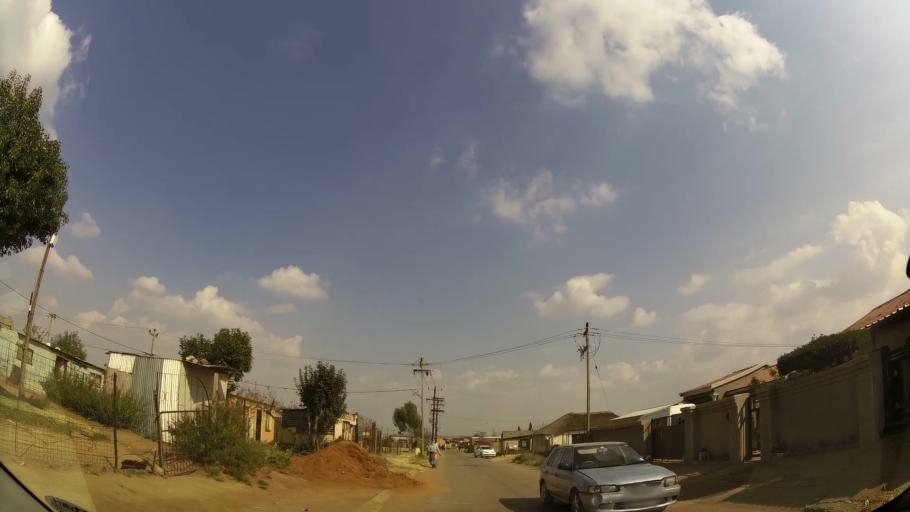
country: ZA
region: Gauteng
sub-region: Ekurhuleni Metropolitan Municipality
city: Springs
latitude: -26.1288
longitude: 28.4829
